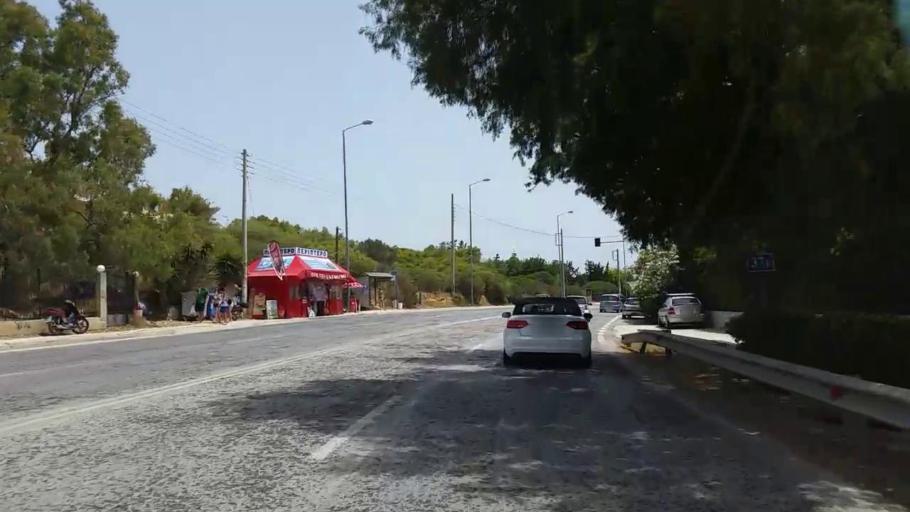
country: GR
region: Attica
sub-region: Nomarchia Anatolikis Attikis
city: Agios Dimitrios Kropias
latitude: 37.8018
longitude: 23.8690
